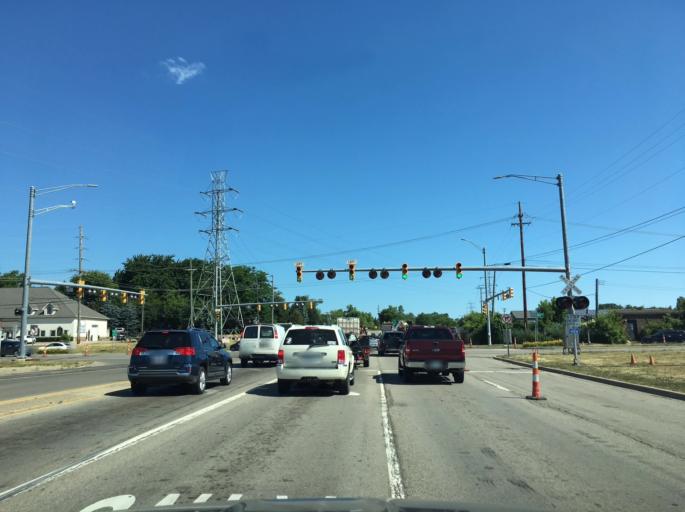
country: US
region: Michigan
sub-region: Oakland County
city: Auburn Hills
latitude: 42.7071
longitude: -83.2852
